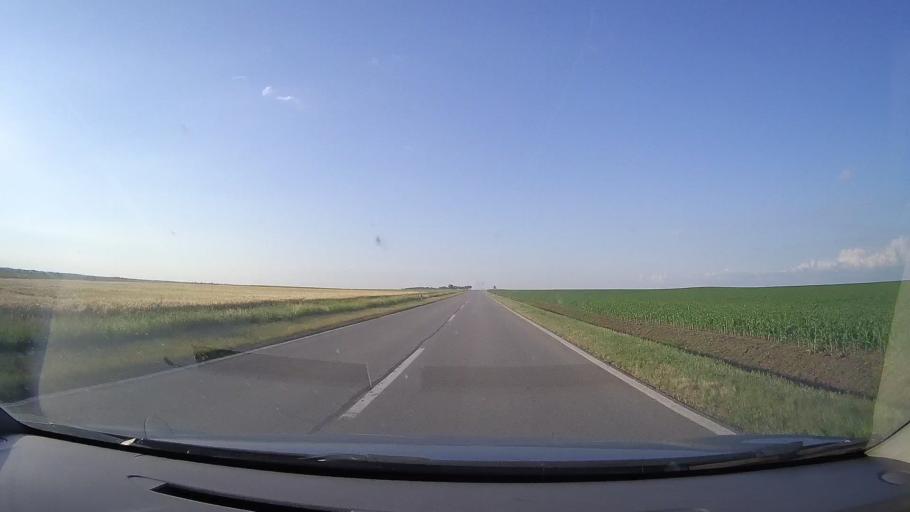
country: RO
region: Timis
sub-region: Comuna Moravita
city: Moravita
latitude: 45.1906
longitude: 21.2985
